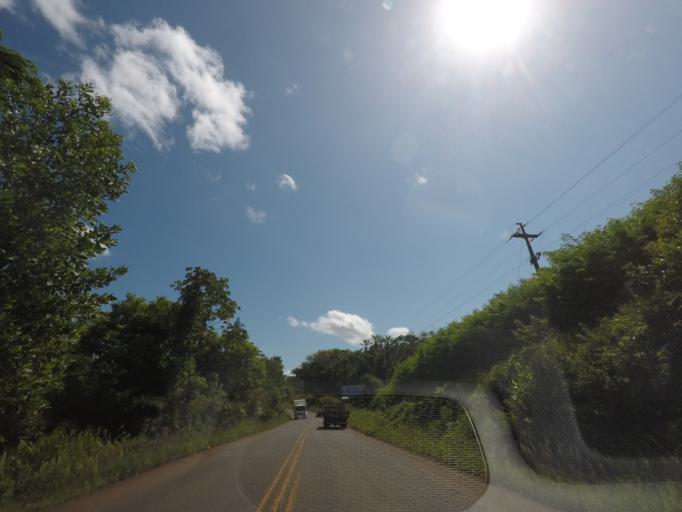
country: BR
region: Bahia
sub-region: Itubera
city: Itubera
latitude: -13.6916
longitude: -39.1330
